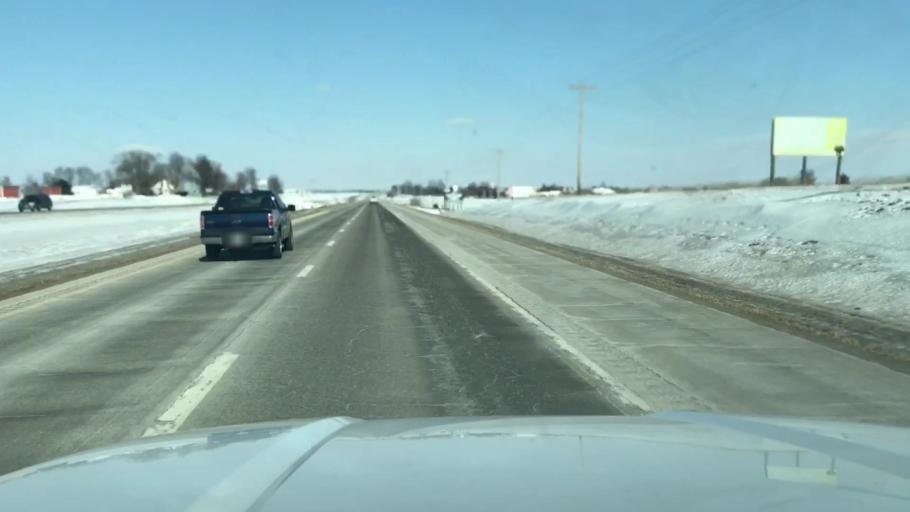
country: US
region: Missouri
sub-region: Nodaway County
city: Maryville
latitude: 40.2856
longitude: -94.8753
